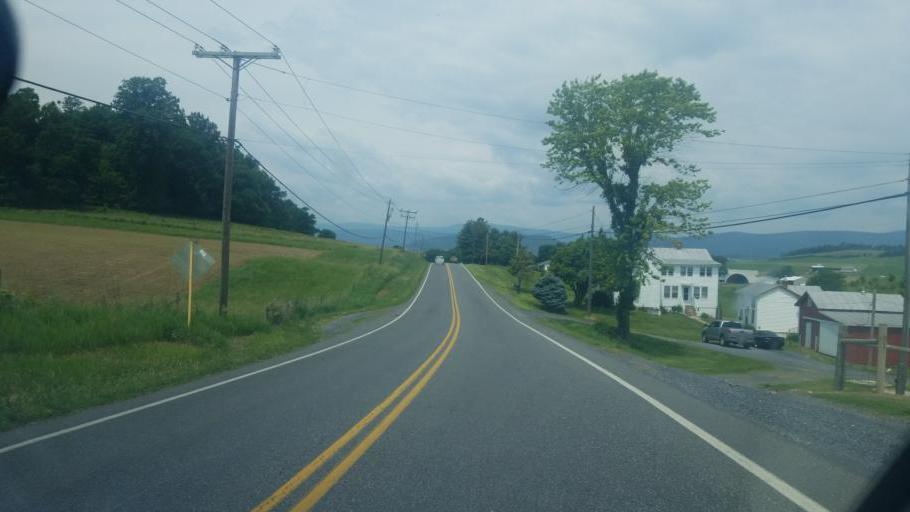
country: US
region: Virginia
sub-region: Rockingham County
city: Dayton
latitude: 38.4637
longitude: -78.9637
